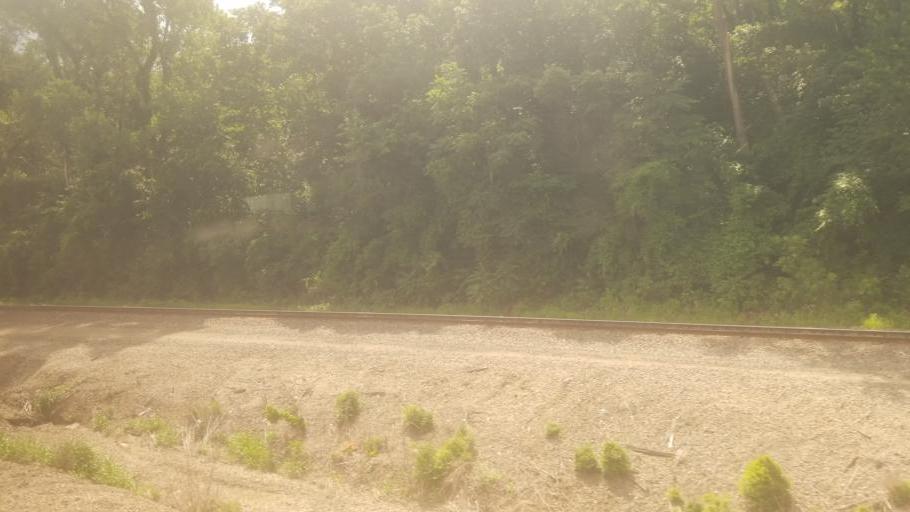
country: US
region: Missouri
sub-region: Jackson County
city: Sugar Creek
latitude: 39.1147
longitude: -94.4693
